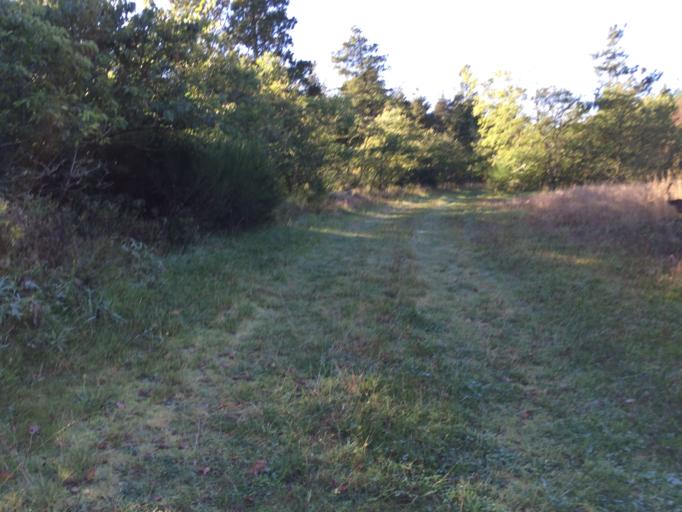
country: DK
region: Central Jutland
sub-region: Holstebro Kommune
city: Ulfborg
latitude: 56.2460
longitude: 8.3684
